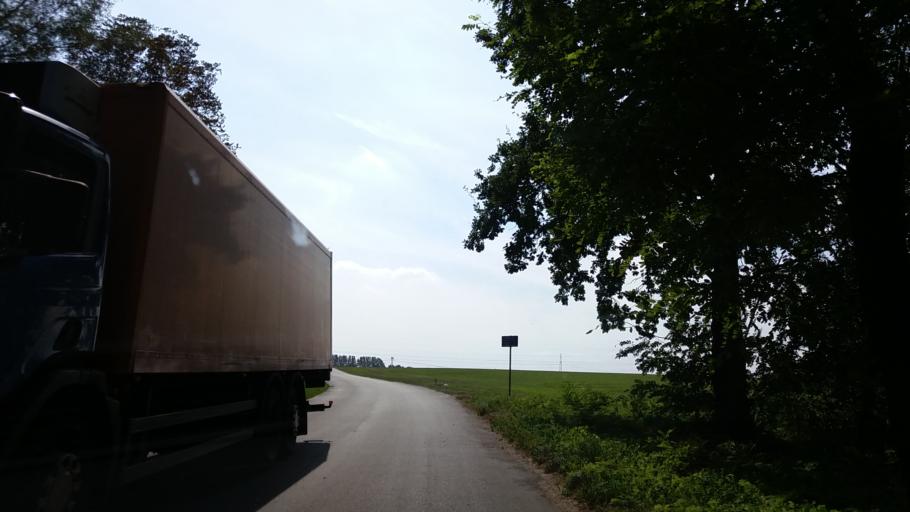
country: PL
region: West Pomeranian Voivodeship
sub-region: Powiat stargardzki
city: Stargard Szczecinski
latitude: 53.3539
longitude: 14.9718
